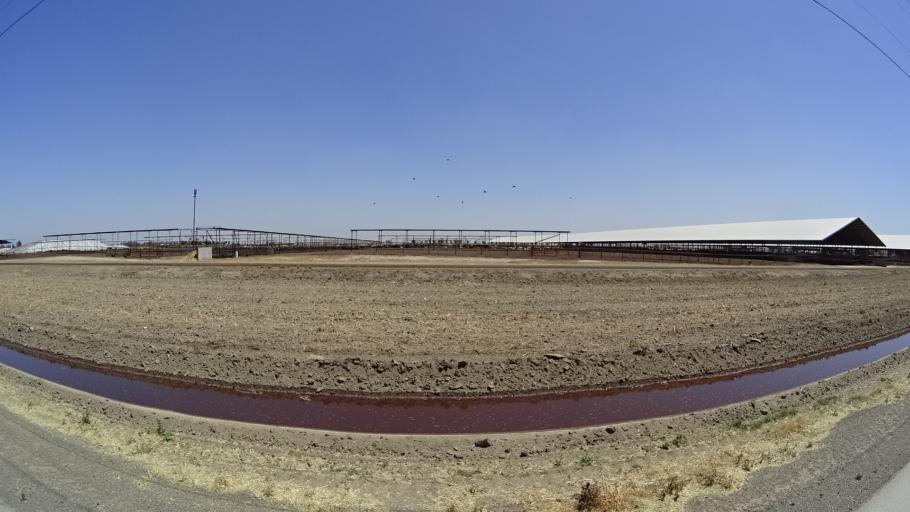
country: US
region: California
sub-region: Kings County
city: Home Garden
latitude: 36.1999
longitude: -119.6459
